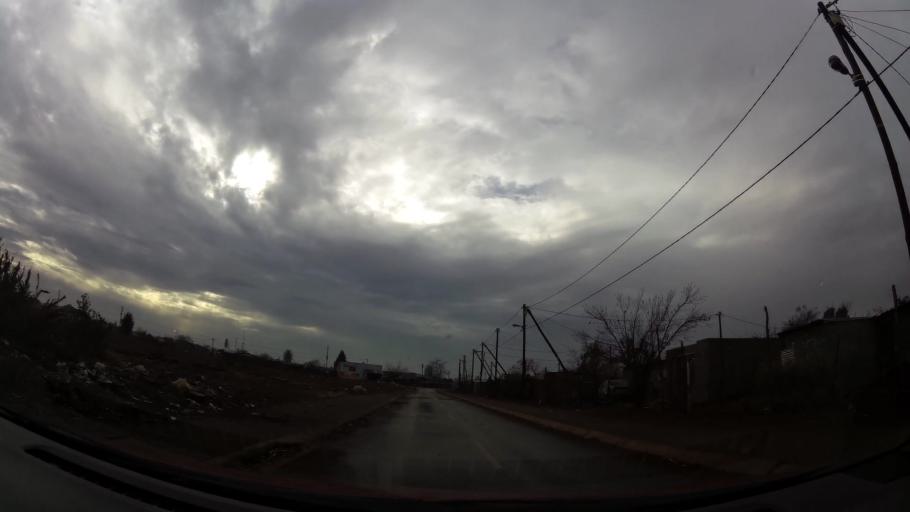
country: ZA
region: Gauteng
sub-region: City of Johannesburg Metropolitan Municipality
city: Soweto
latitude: -26.2850
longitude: 27.8392
